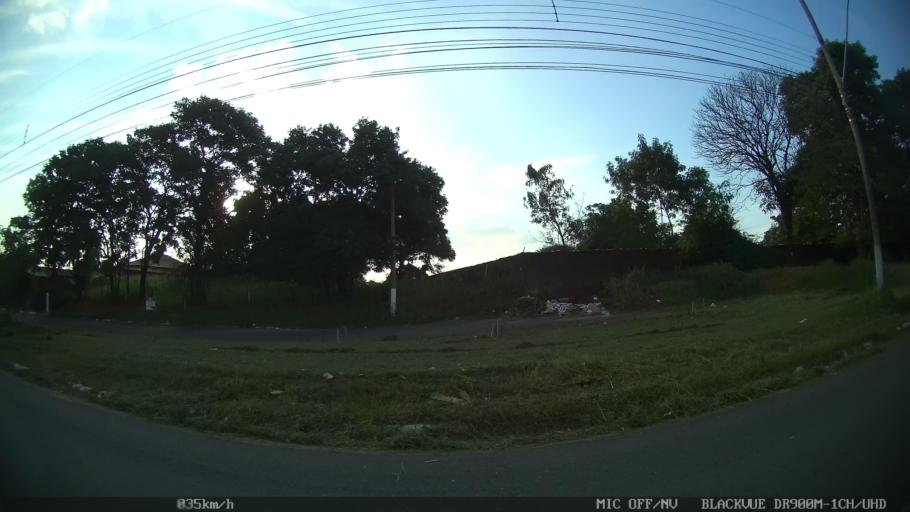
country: BR
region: Sao Paulo
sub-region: Hortolandia
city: Hortolandia
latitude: -22.8861
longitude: -47.1634
